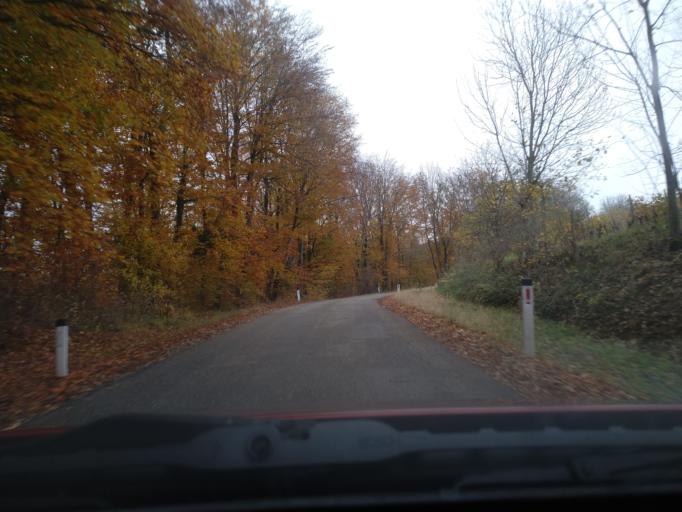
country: SI
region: Sentilj
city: Sentilj v Slov. Goricah
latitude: 46.6779
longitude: 15.6099
